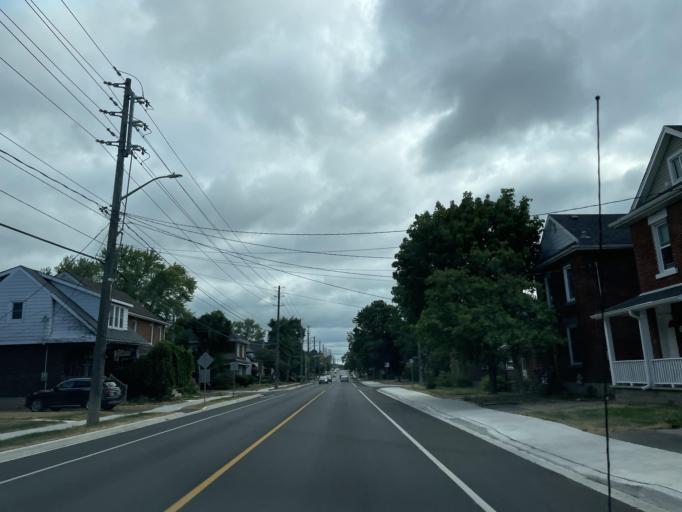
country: CA
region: Ontario
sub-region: Wellington County
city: Guelph
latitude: 43.5476
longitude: -80.2297
